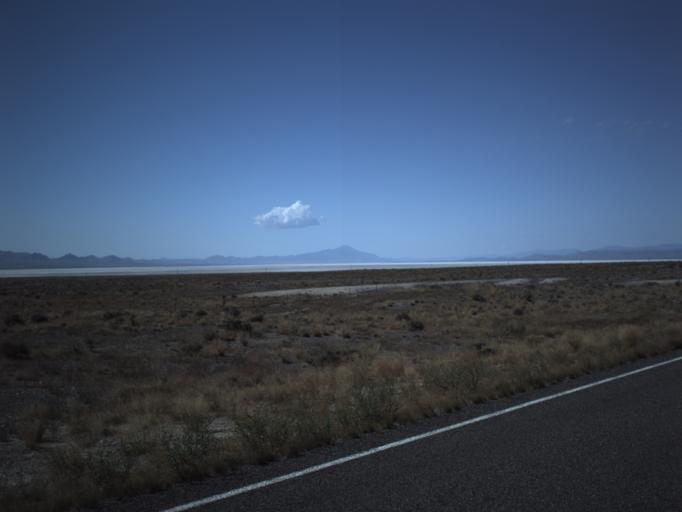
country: US
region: Utah
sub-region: Millard County
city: Delta
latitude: 39.1586
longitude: -113.0550
